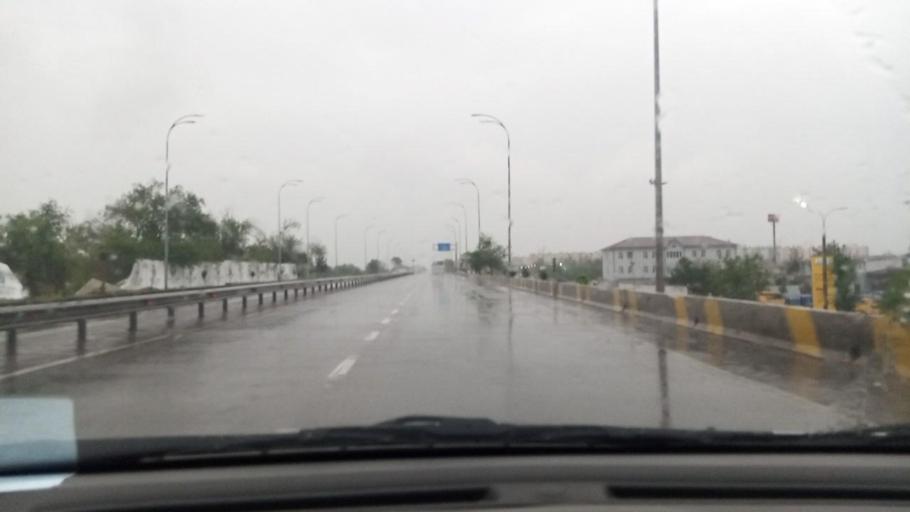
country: UZ
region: Toshkent Shahri
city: Bektemir
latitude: 41.2632
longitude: 69.3723
